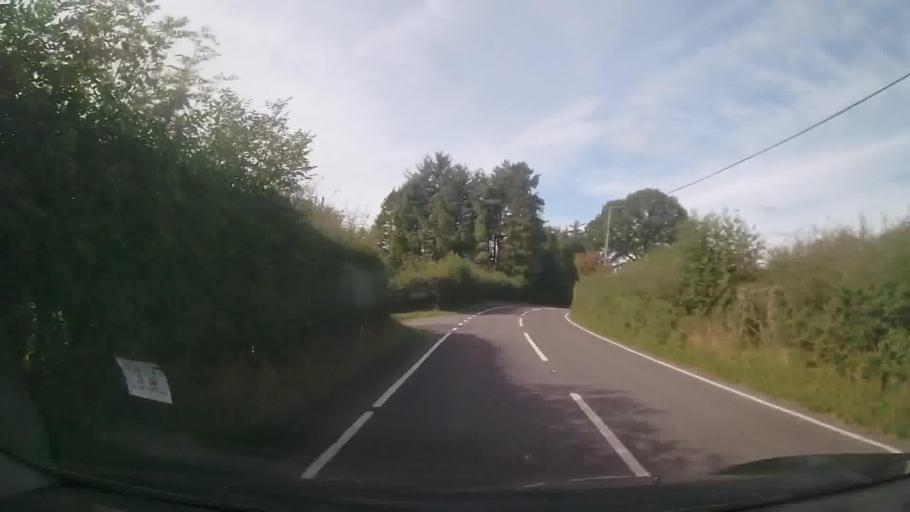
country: GB
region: England
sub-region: Shropshire
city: Lydham
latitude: 52.5674
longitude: -2.9996
